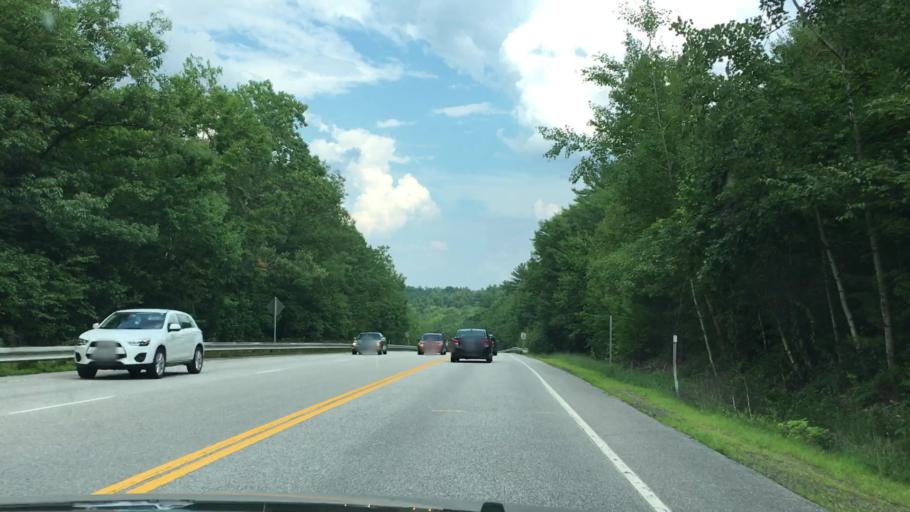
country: US
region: New Hampshire
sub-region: Belknap County
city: Gilford
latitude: 43.5737
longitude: -71.3609
